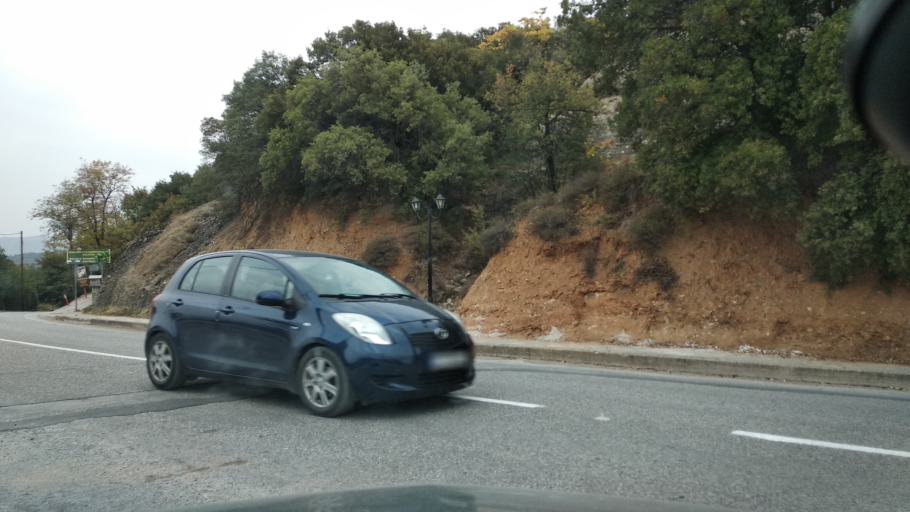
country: GR
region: Thessaly
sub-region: Trikala
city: Kastraki
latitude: 39.7096
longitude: 21.6168
